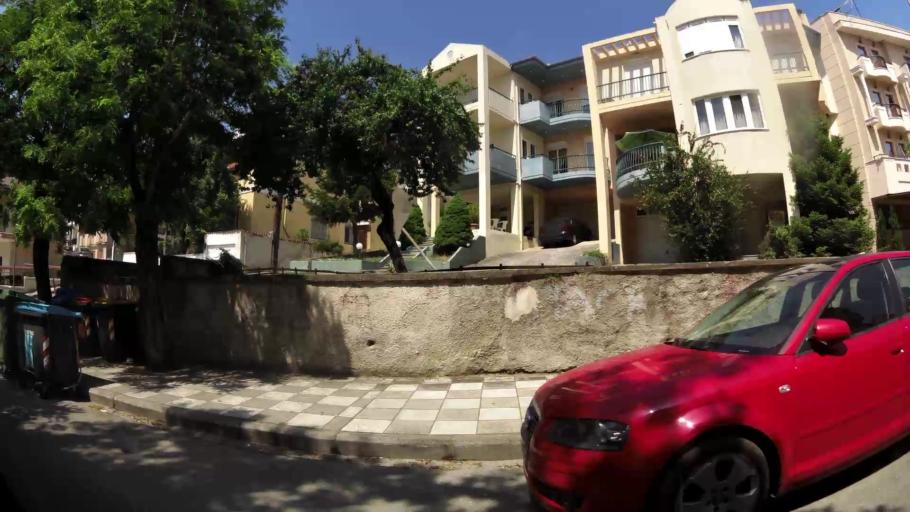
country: GR
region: West Macedonia
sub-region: Nomos Kozanis
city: Kozani
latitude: 40.3073
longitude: 21.7838
